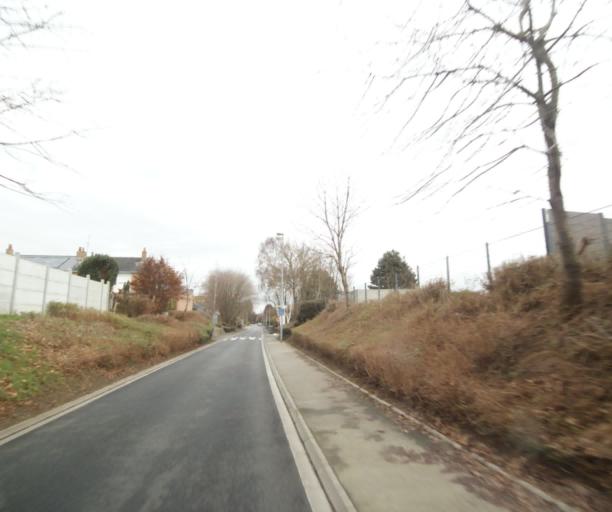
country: FR
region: Nord-Pas-de-Calais
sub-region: Departement du Nord
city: Saint-Saulve
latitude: 50.3651
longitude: 3.5632
